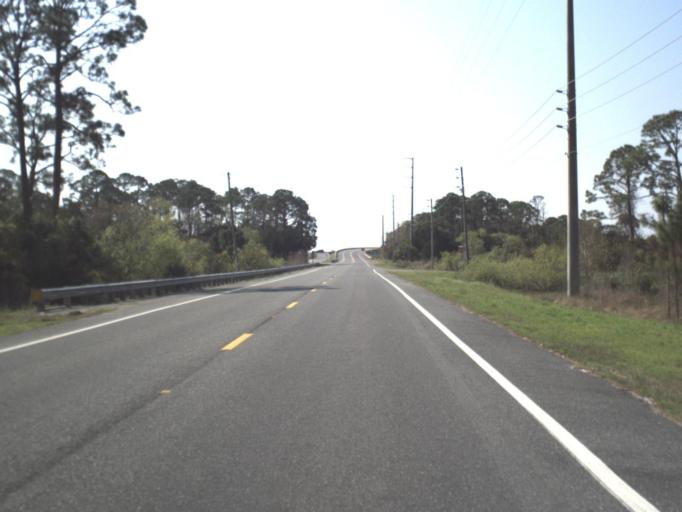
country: US
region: Florida
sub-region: Franklin County
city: Eastpoint
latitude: 29.7284
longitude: -84.8880
